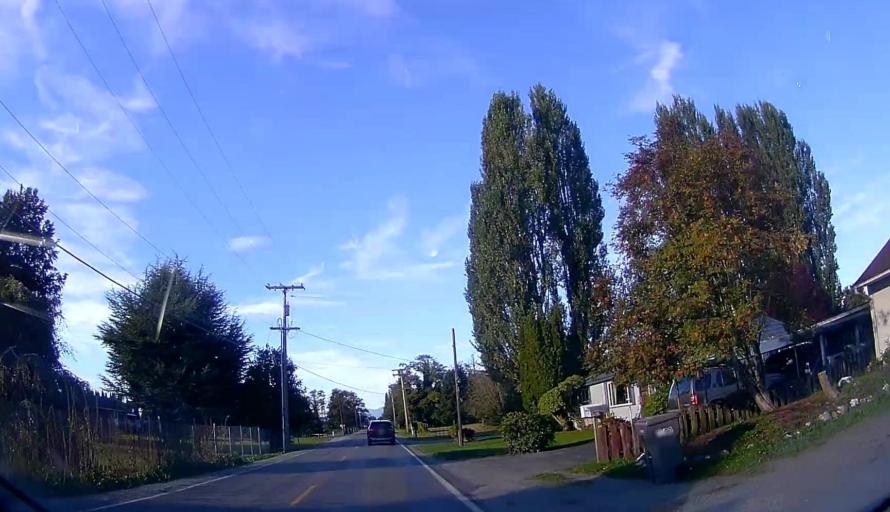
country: US
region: Washington
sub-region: Skagit County
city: Burlington
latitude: 48.4576
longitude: -122.3571
